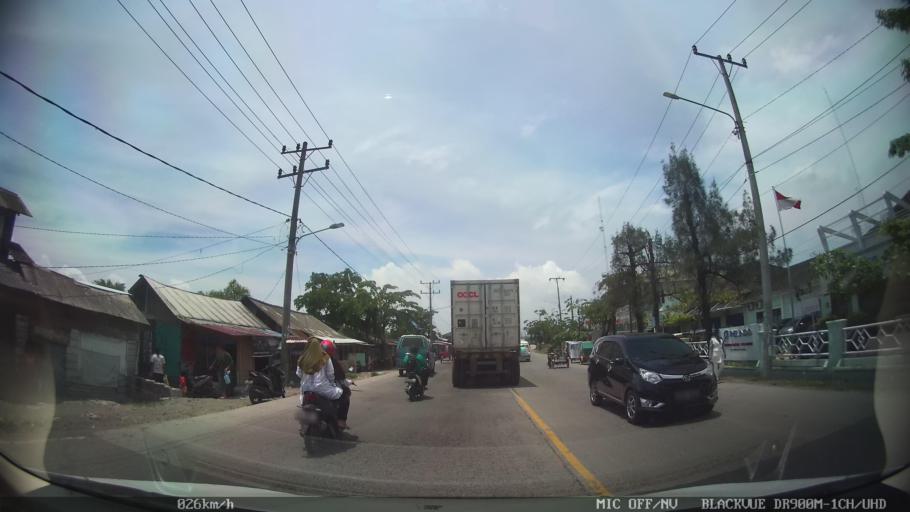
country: ID
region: North Sumatra
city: Belawan
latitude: 3.7652
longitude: 98.6826
